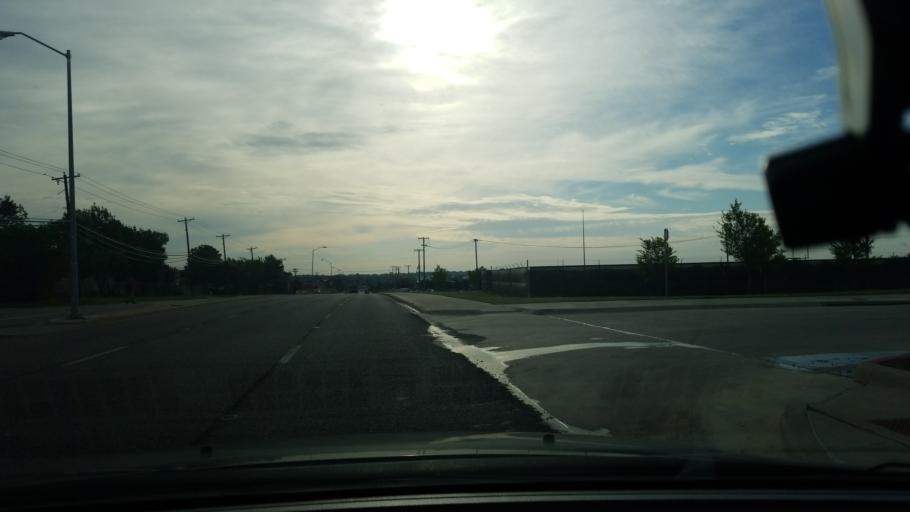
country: US
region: Texas
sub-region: Dallas County
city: Mesquite
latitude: 32.7658
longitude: -96.6328
